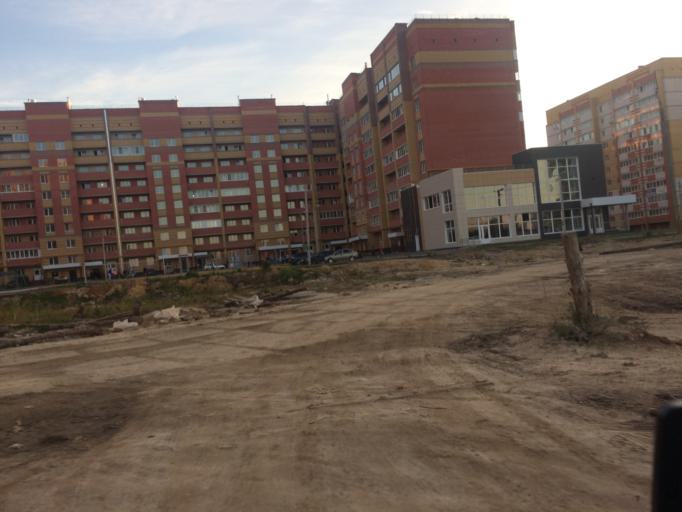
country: RU
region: Mariy-El
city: Yoshkar-Ola
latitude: 56.6398
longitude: 47.9309
